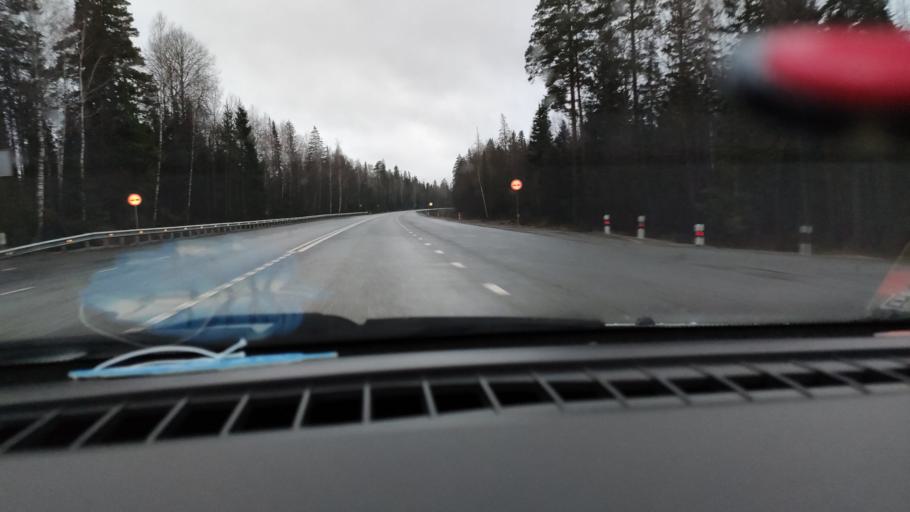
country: RU
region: Udmurtiya
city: Alnashi
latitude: 56.0882
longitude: 52.4387
